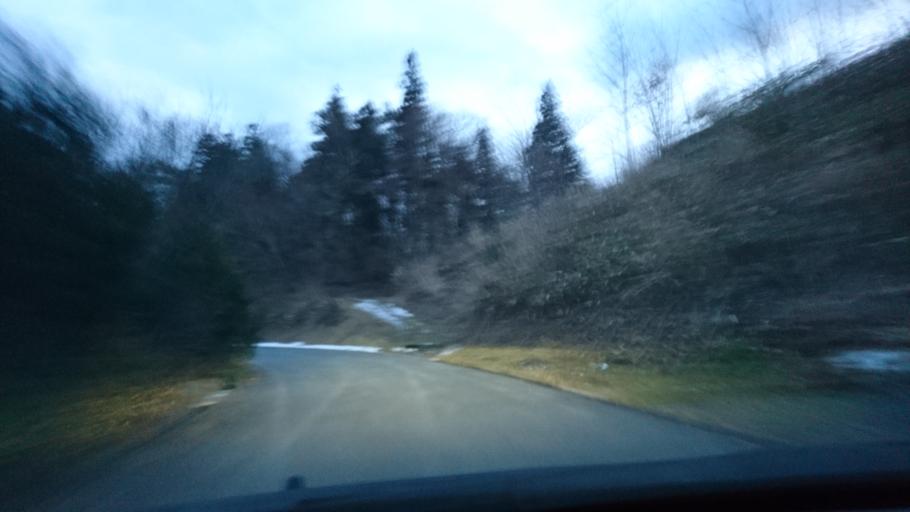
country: JP
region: Iwate
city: Ichinoseki
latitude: 38.9074
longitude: 141.3466
